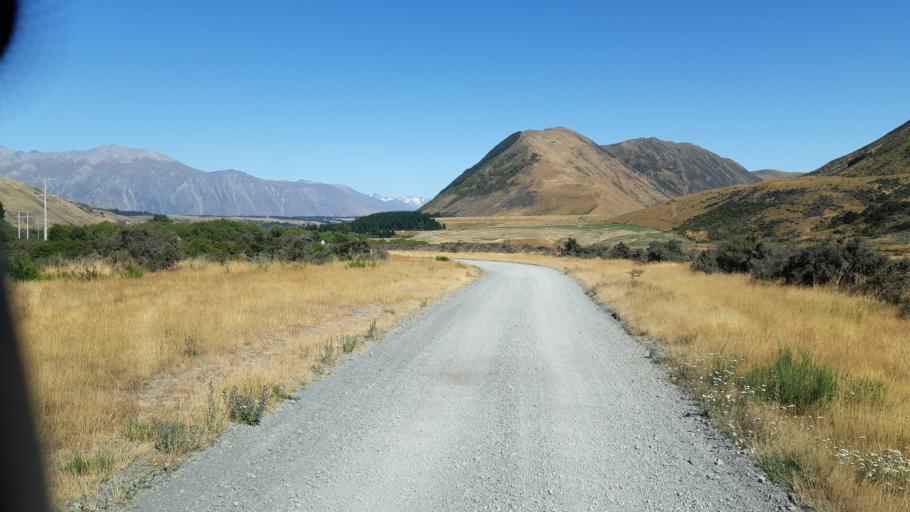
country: NZ
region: Canterbury
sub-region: Ashburton District
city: Methven
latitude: -43.3411
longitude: 171.6066
